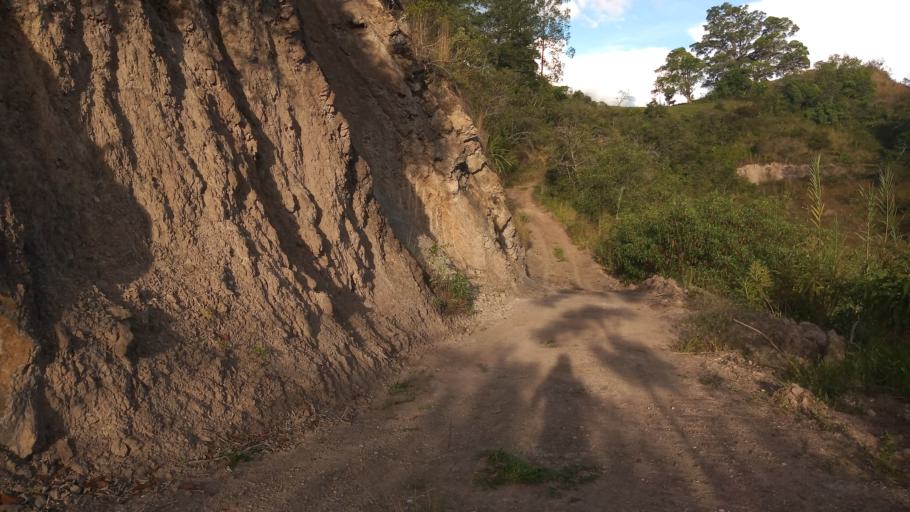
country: CO
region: Cundinamarca
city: Tenza
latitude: 5.0716
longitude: -73.3926
